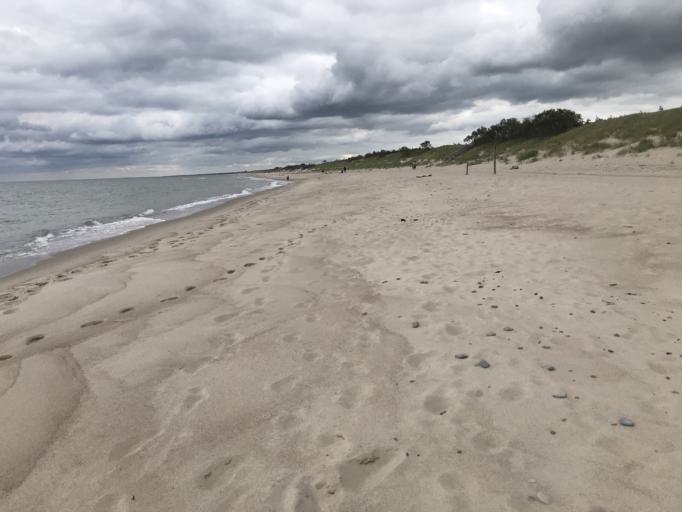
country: LT
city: Nida
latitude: 55.2483
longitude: 20.9197
